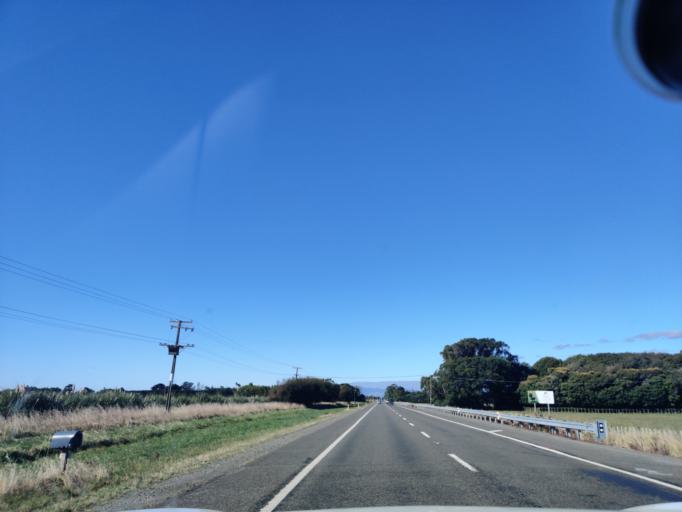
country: NZ
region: Manawatu-Wanganui
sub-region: Palmerston North City
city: Palmerston North
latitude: -40.3984
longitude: 175.5101
